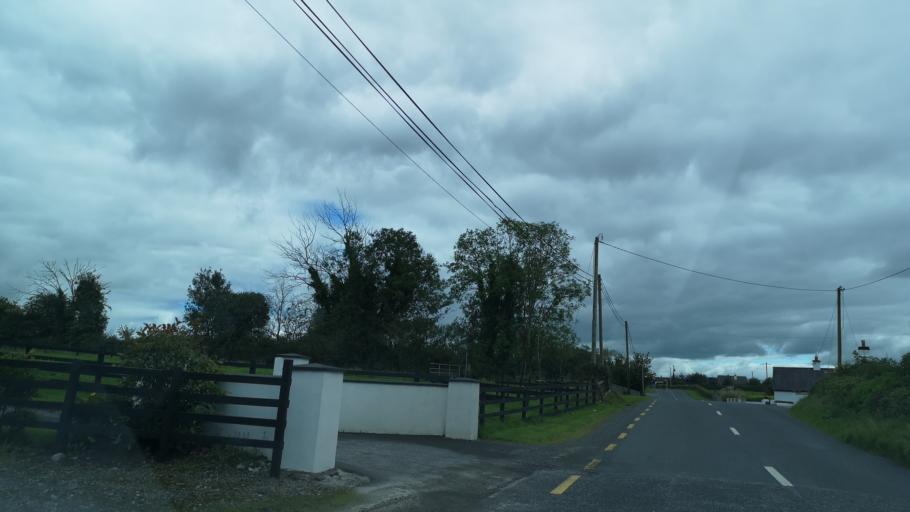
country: IE
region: Connaught
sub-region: County Galway
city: Ballinasloe
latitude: 53.3019
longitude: -8.1303
